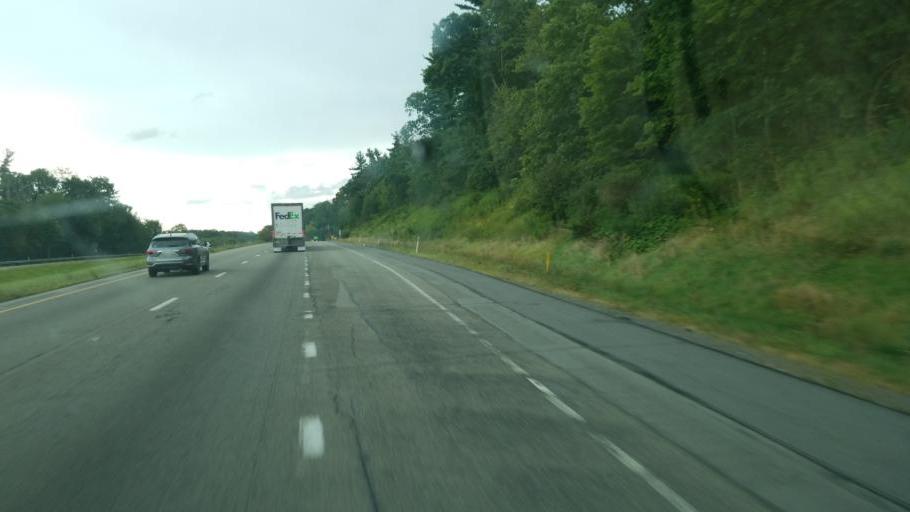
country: US
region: Pennsylvania
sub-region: Clarion County
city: Knox
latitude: 41.1813
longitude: -79.6835
